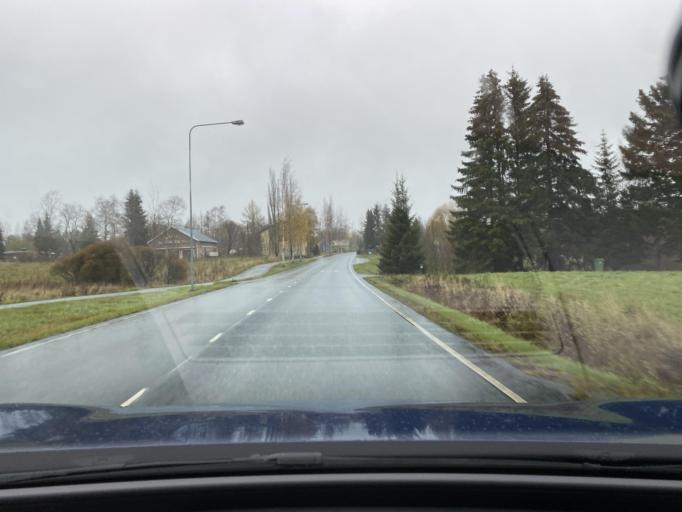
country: FI
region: Varsinais-Suomi
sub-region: Loimaa
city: Alastaro
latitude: 60.9453
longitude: 22.8653
